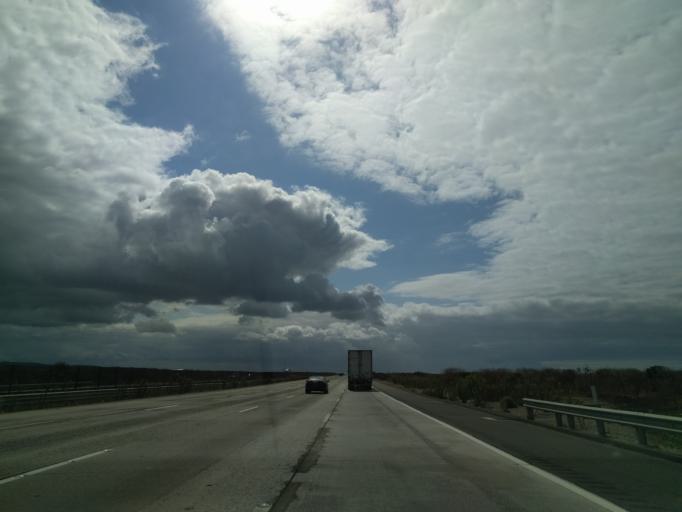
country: US
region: California
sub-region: San Diego County
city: Camp Pendleton South
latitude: 33.3041
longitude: -117.4715
